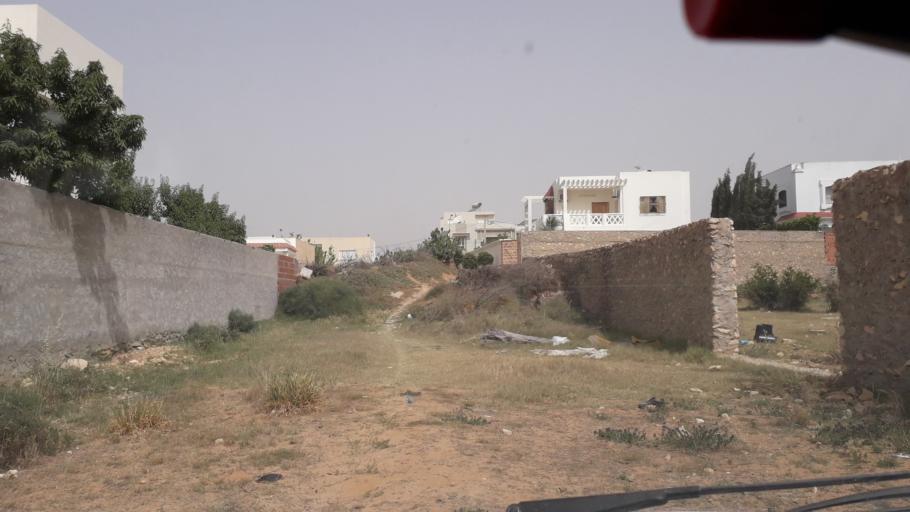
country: TN
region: Safaqis
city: Al Qarmadah
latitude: 34.8031
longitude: 10.7726
